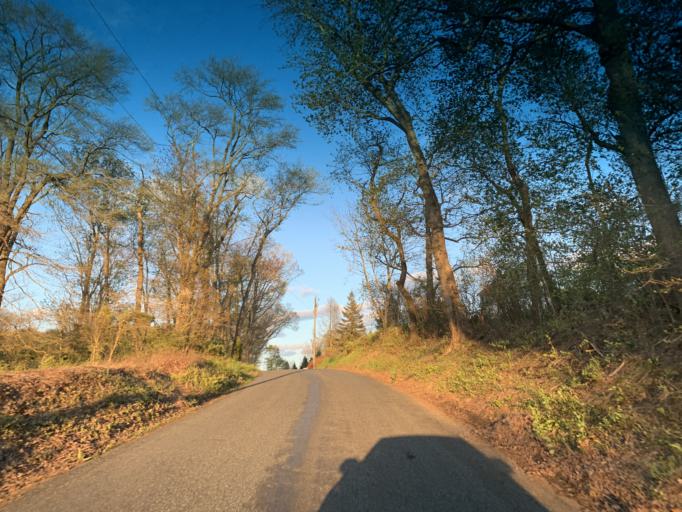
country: US
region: Maryland
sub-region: Harford County
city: Jarrettsville
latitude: 39.6561
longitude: -76.4305
